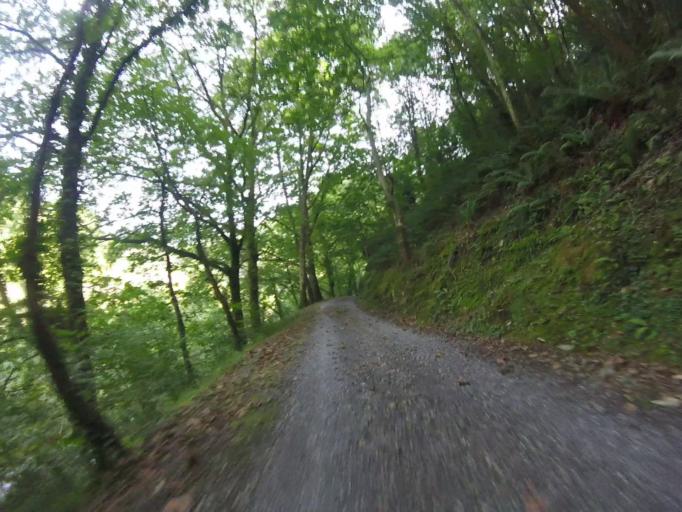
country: ES
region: Navarre
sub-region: Provincia de Navarra
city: Arano
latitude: 43.2243
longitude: -1.9311
